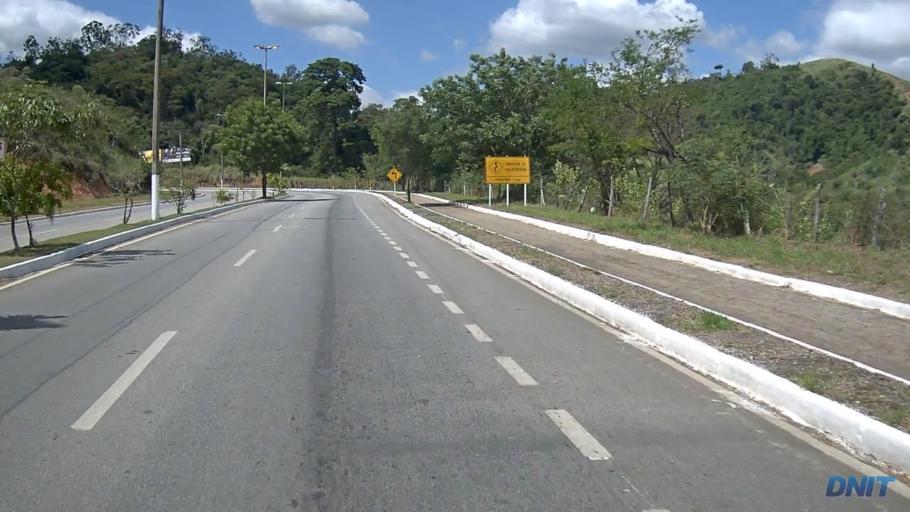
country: BR
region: Minas Gerais
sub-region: Coronel Fabriciano
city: Coronel Fabriciano
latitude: -19.5050
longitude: -42.5950
